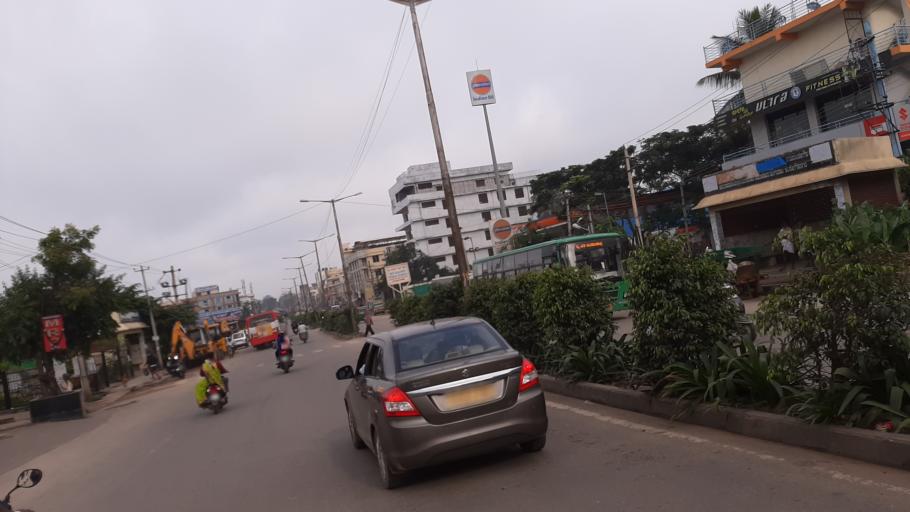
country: IN
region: Karnataka
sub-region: Bangalore Urban
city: Bangalore
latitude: 12.9860
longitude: 77.4782
